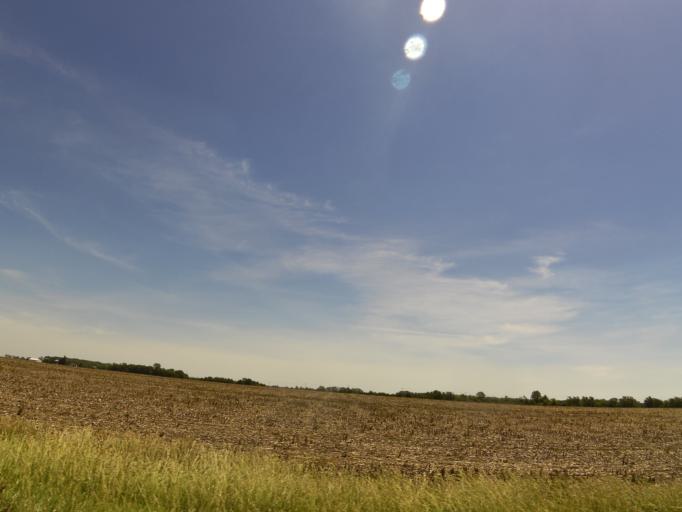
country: US
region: Illinois
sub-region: Vermilion County
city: Rossville
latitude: 40.3416
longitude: -87.6630
